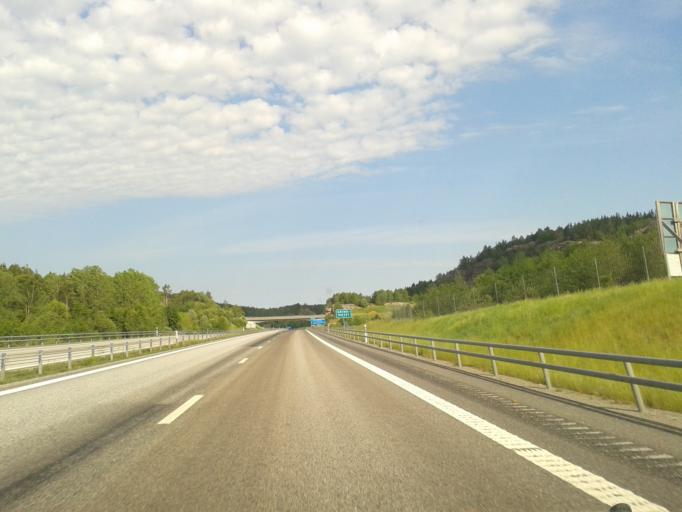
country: SE
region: Vaestra Goetaland
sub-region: Lysekils Kommun
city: Brastad
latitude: 58.5578
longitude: 11.4913
